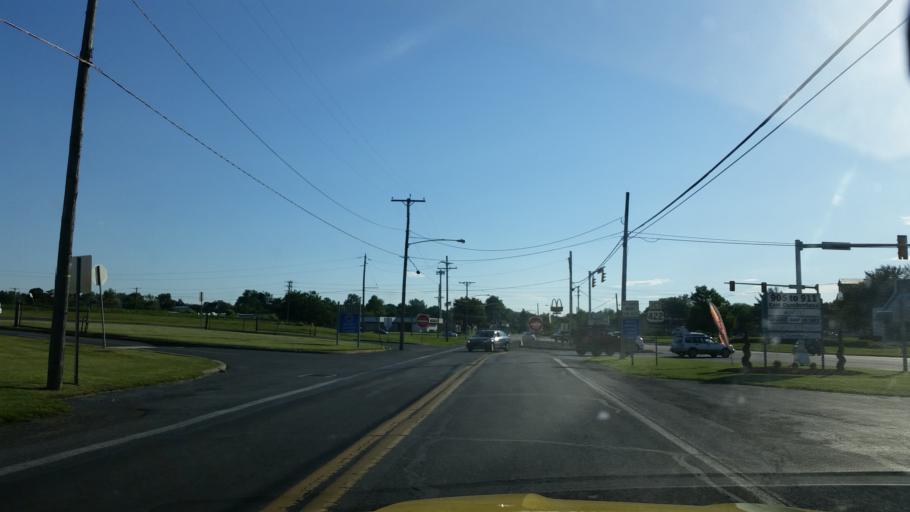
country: US
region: Pennsylvania
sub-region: Lebanon County
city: Avon
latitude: 40.3437
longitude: -76.3948
